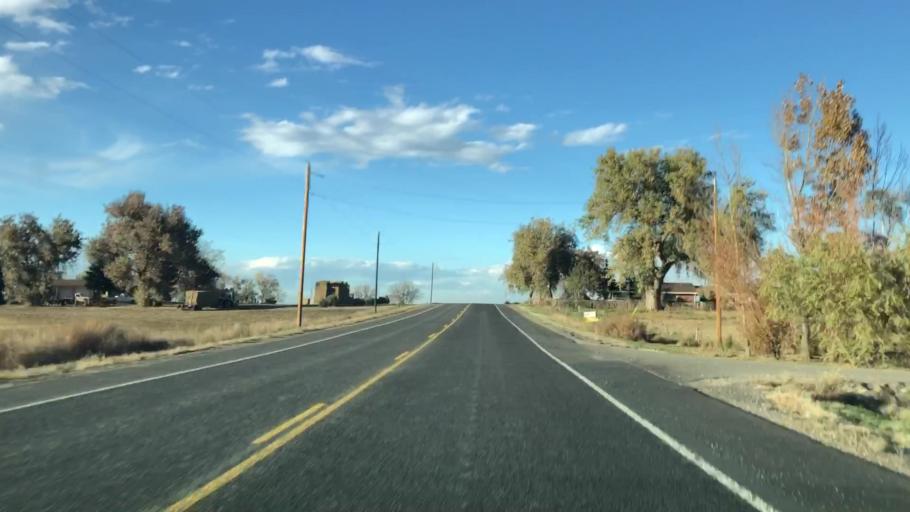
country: US
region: Colorado
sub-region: Larimer County
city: Loveland
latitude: 40.4709
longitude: -105.0203
